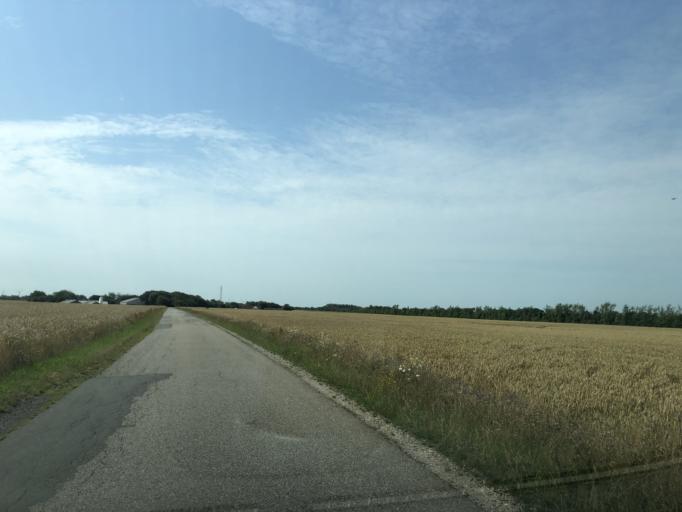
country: DK
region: Central Jutland
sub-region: Lemvig Kommune
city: Lemvig
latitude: 56.4436
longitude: 8.2894
